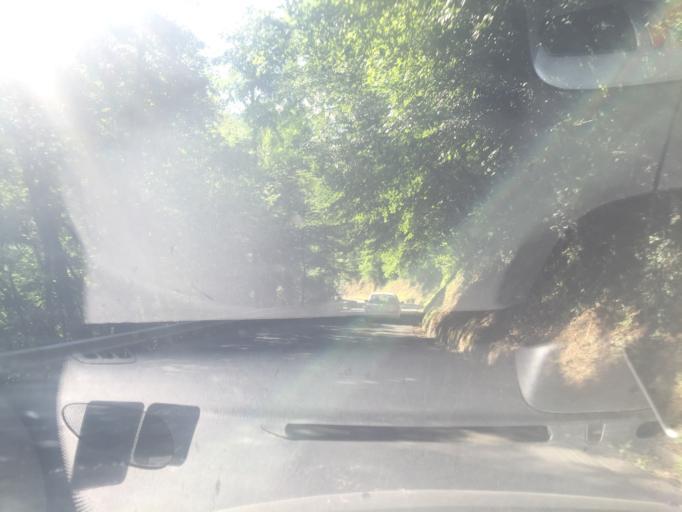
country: IT
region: Tuscany
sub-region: Provincia di Lucca
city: Careggine
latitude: 44.1326
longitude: 10.3065
